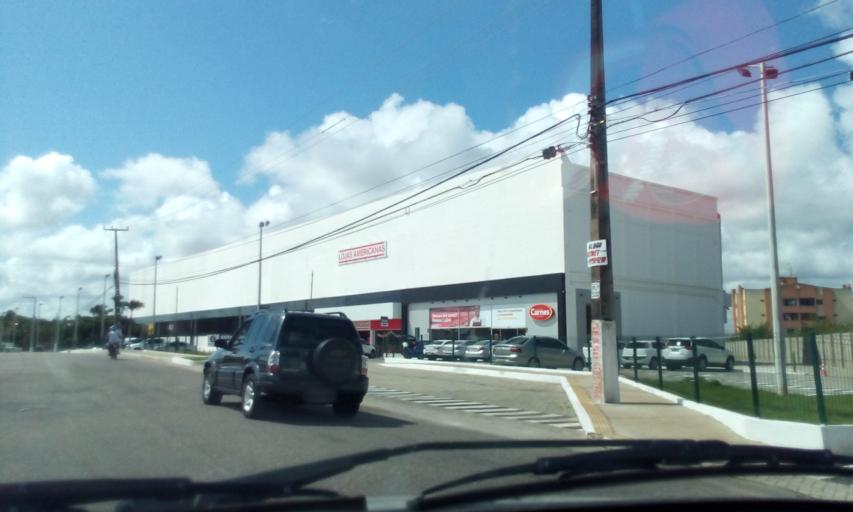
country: BR
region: Rio Grande do Norte
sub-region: Parnamirim
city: Parnamirim
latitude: -5.8956
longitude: -35.1981
